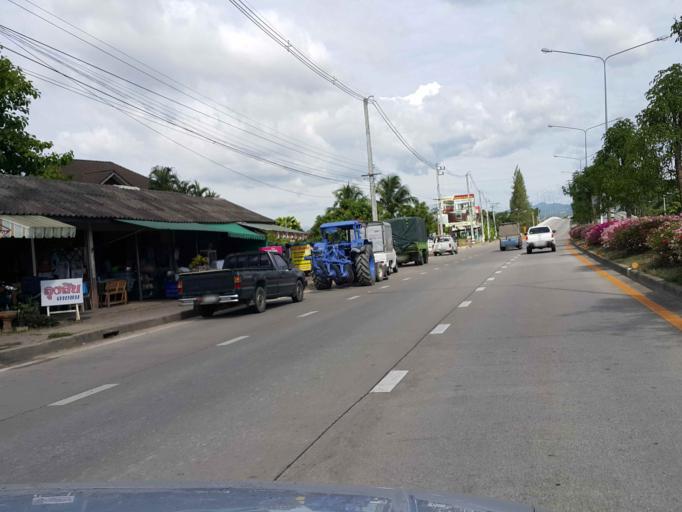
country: TH
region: Chiang Mai
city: Chiang Mai
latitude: 18.7449
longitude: 98.9889
